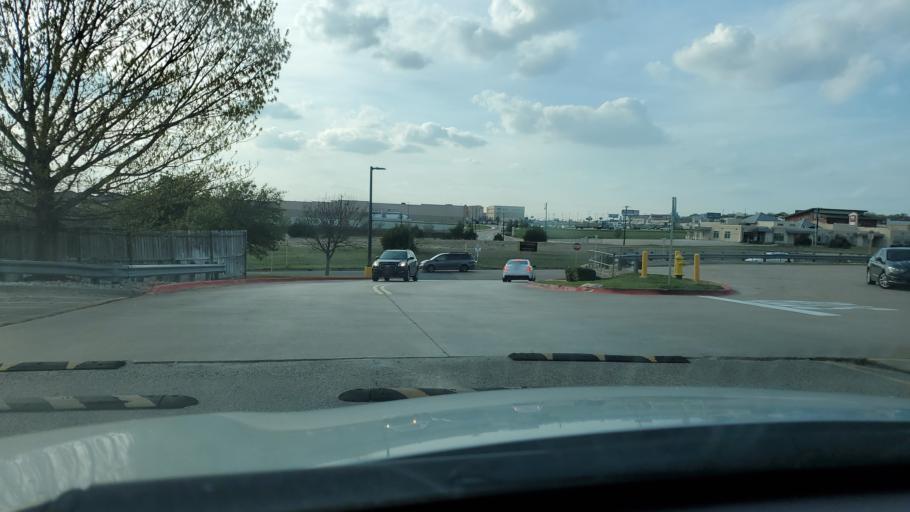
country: US
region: Texas
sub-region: Bell County
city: Harker Heights
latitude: 31.0693
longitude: -97.6751
